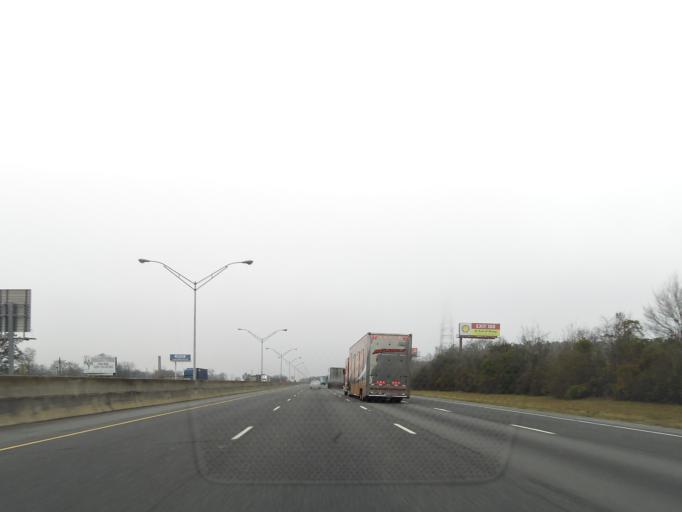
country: US
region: Georgia
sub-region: Monroe County
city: Forsyth
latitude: 33.0483
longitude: -83.9447
